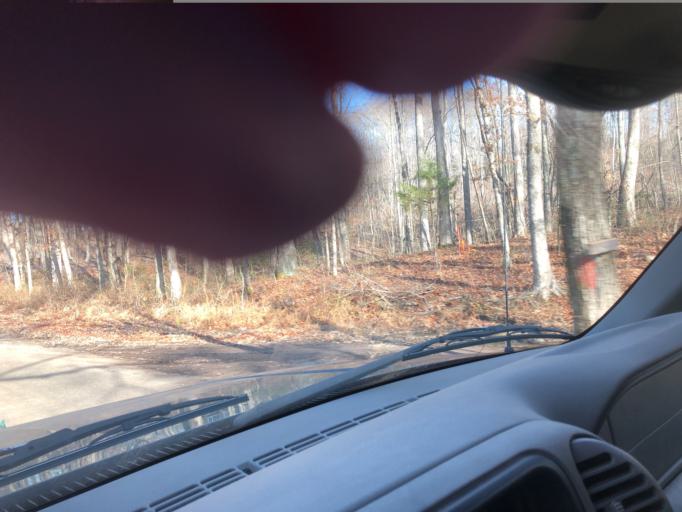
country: US
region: Tennessee
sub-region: Putnam County
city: Monterey
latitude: 35.9952
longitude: -85.2776
